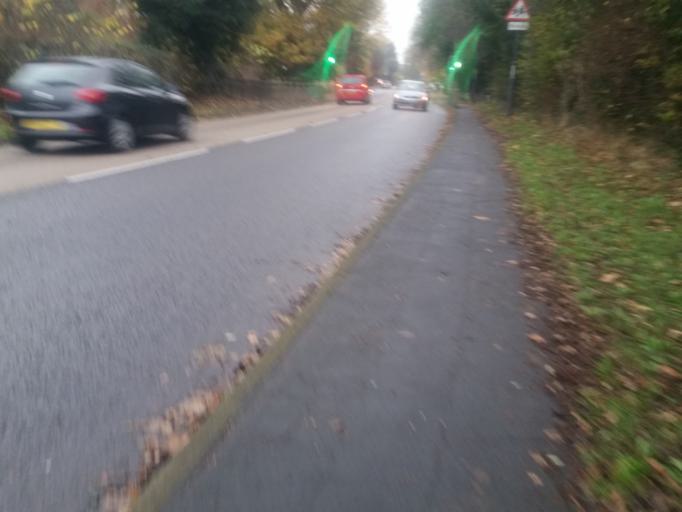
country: GB
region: England
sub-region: Derbyshire
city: Borrowash
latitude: 52.8896
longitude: -1.4172
